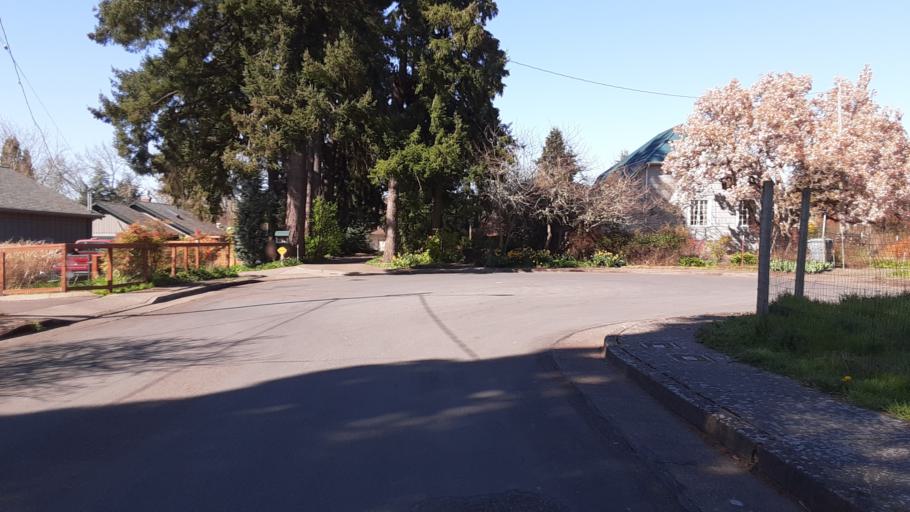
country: US
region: Oregon
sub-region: Benton County
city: Corvallis
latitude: 44.5463
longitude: -123.2608
